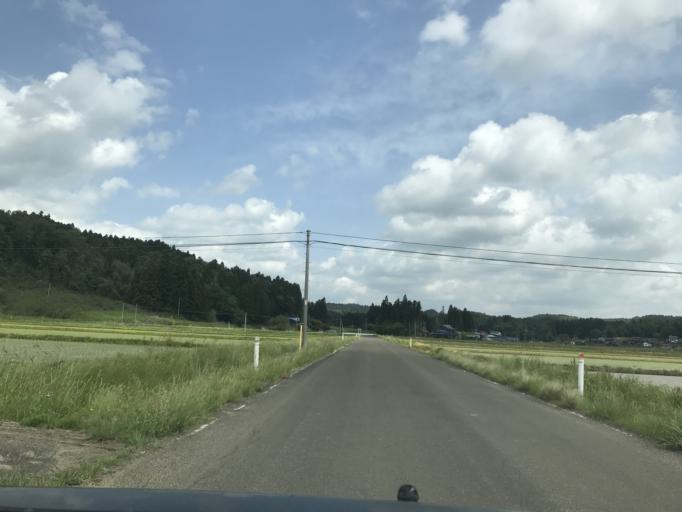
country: JP
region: Iwate
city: Ichinoseki
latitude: 38.8407
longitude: 141.0184
